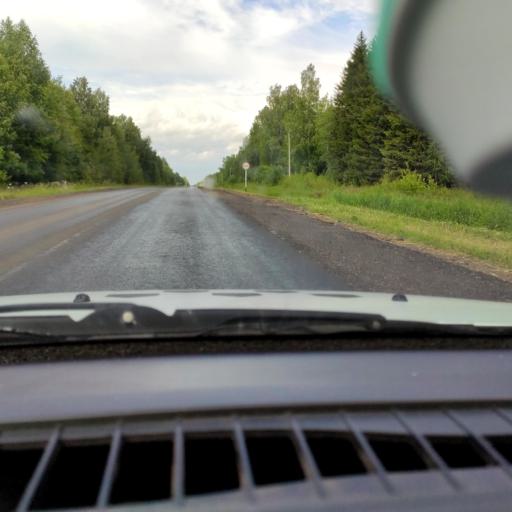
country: RU
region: Perm
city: Orda
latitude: 57.2226
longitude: 56.9538
